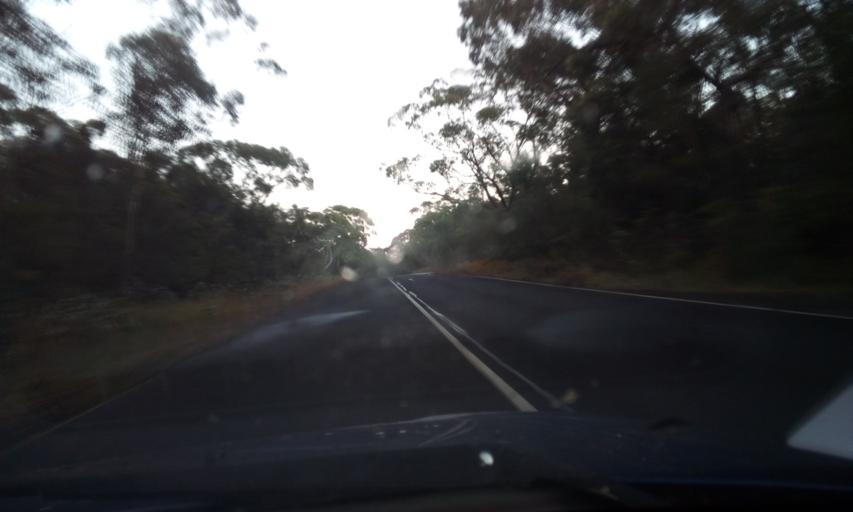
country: AU
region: New South Wales
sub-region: Wollongong
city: Mount Keira
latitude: -34.3835
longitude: 150.8363
